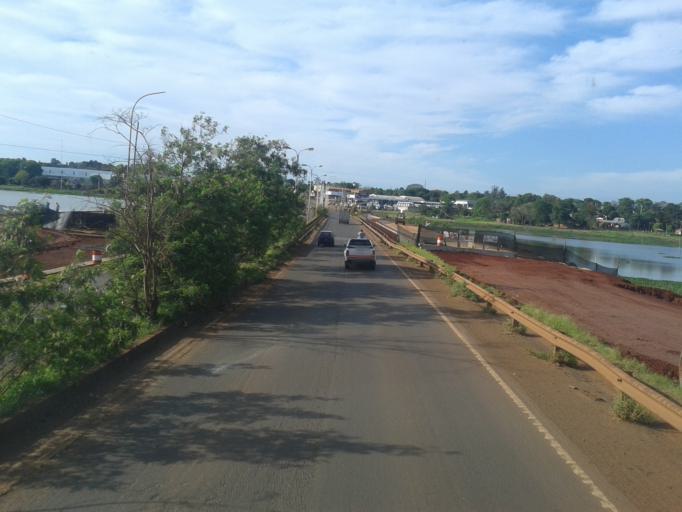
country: AR
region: Misiones
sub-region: Departamento de Capital
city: Posadas
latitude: -27.4177
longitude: -55.9004
